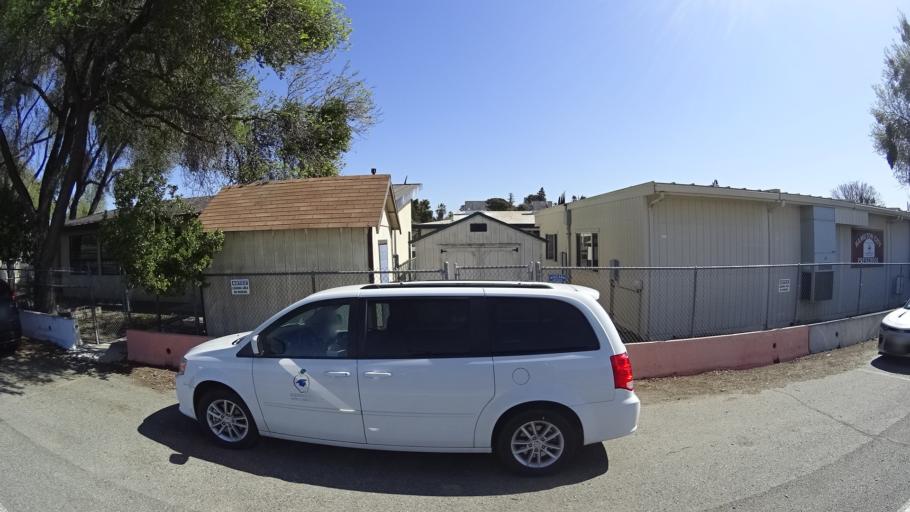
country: US
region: California
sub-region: Glenn County
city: Hamilton City
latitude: 39.7397
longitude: -122.0170
